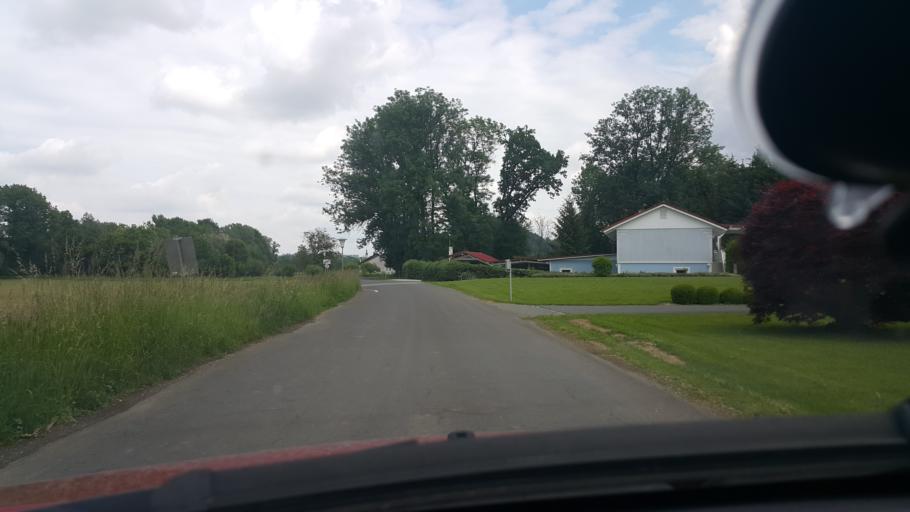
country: AT
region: Styria
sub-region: Politischer Bezirk Leibnitz
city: Weitendorf
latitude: 46.8812
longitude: 15.4817
